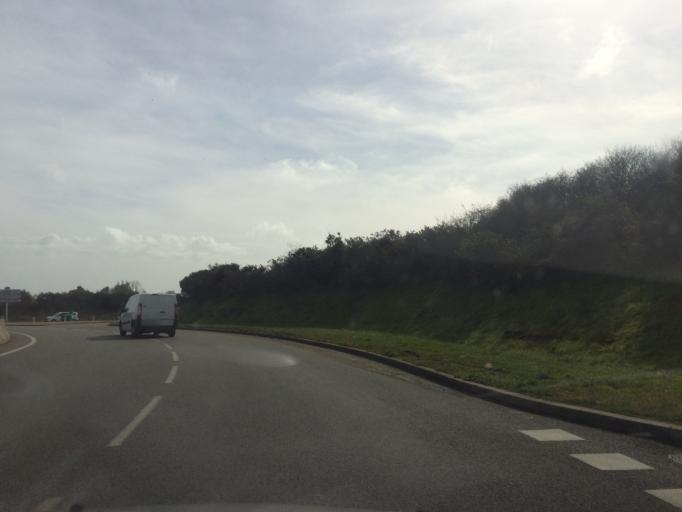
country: FR
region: Pays de la Loire
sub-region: Departement de la Loire-Atlantique
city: Saint-Nazaire
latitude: 47.2859
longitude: -2.2513
